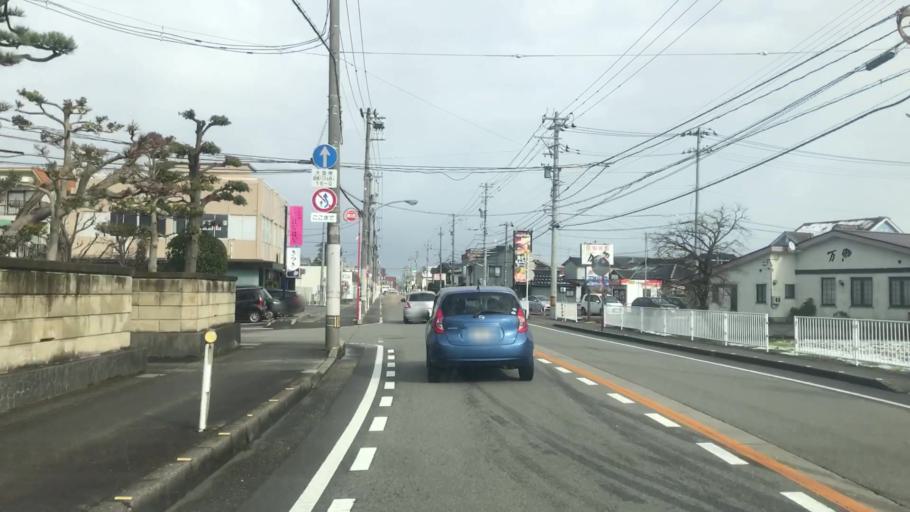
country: JP
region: Toyama
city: Toyama-shi
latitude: 36.6572
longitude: 137.2188
